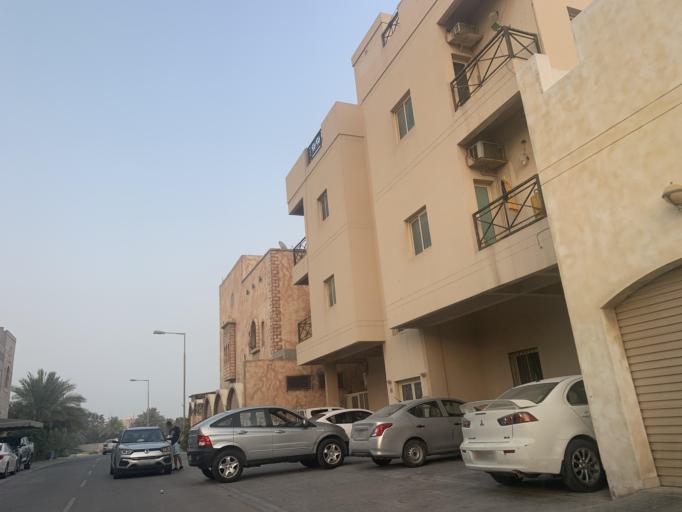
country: BH
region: Manama
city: Jidd Hafs
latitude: 26.2251
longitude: 50.5132
